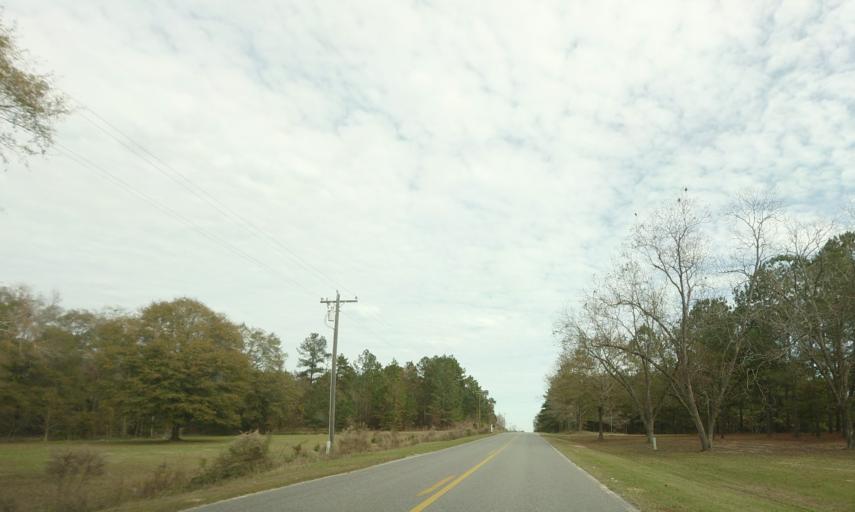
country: US
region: Georgia
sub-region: Dodge County
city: Chester
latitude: 32.4340
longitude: -83.1716
